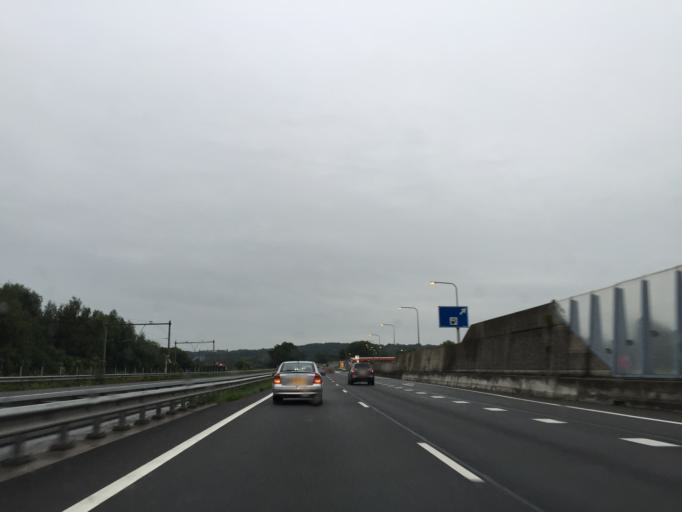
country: NL
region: Limburg
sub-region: Gemeente Meerssen
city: Meerssen
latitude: 50.8837
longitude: 5.7375
